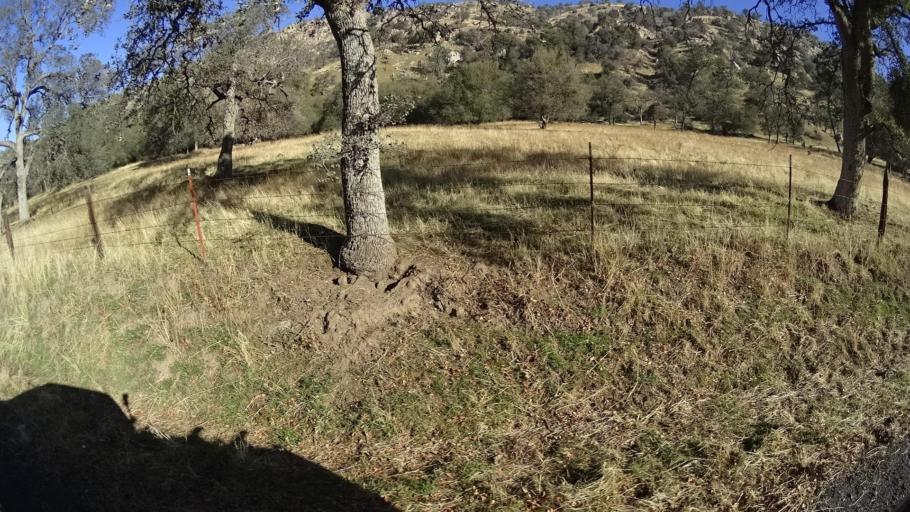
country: US
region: California
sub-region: Kern County
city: Alta Sierra
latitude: 35.7867
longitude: -118.7885
